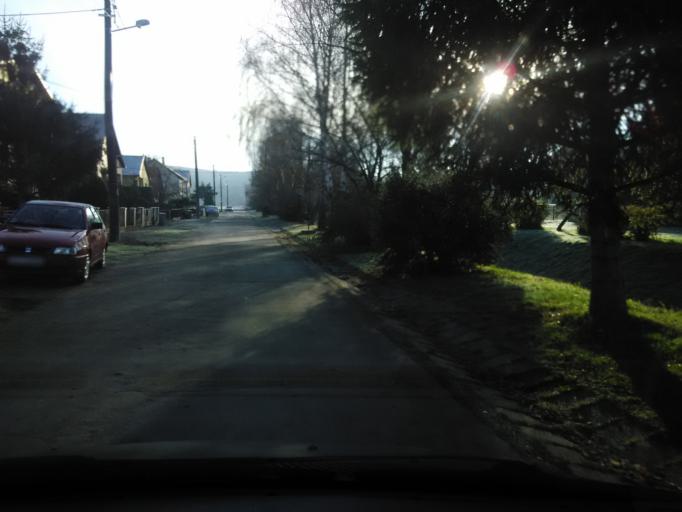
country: SK
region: Nitriansky
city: Tlmace
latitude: 48.3160
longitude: 18.5305
